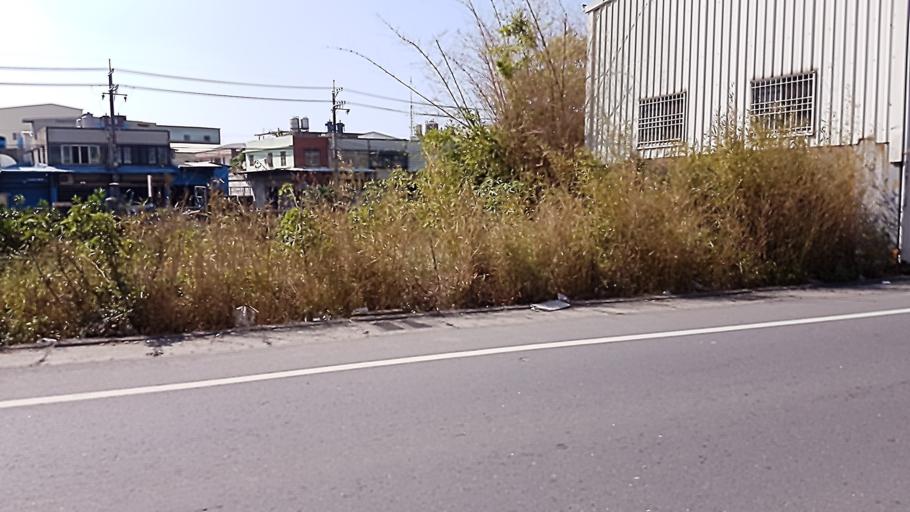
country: TW
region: Taiwan
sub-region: Changhua
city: Chang-hua
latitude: 24.0848
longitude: 120.4844
